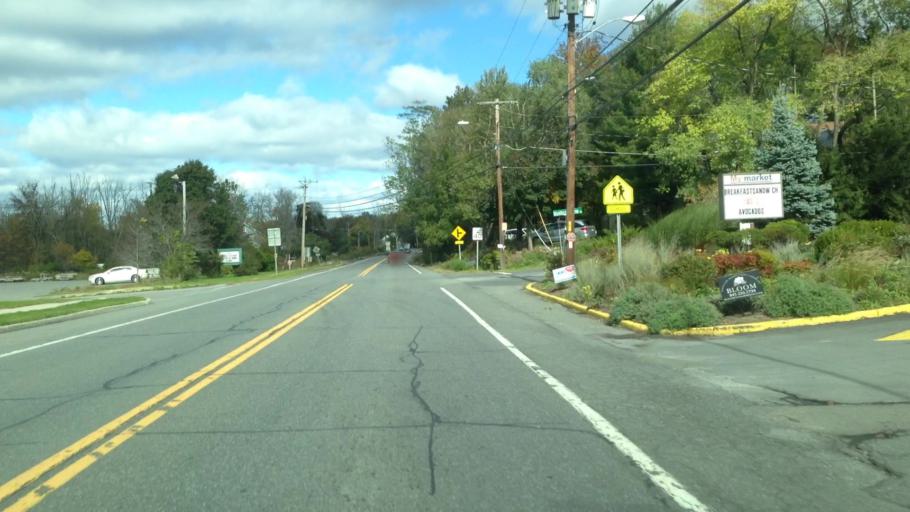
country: US
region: New York
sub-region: Ulster County
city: New Paltz
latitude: 41.7582
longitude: -74.0822
